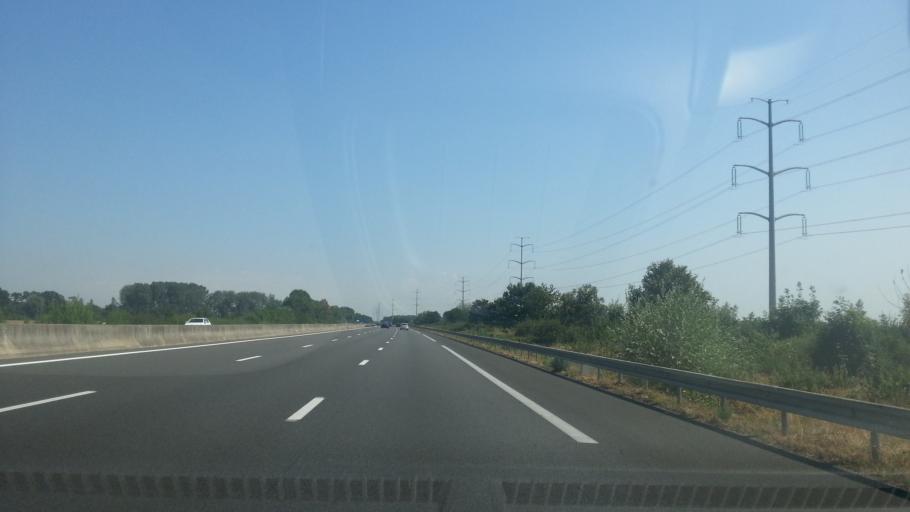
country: FR
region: Centre
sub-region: Departement du Loiret
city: Meung-sur-Loire
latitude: 47.8588
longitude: 1.7057
